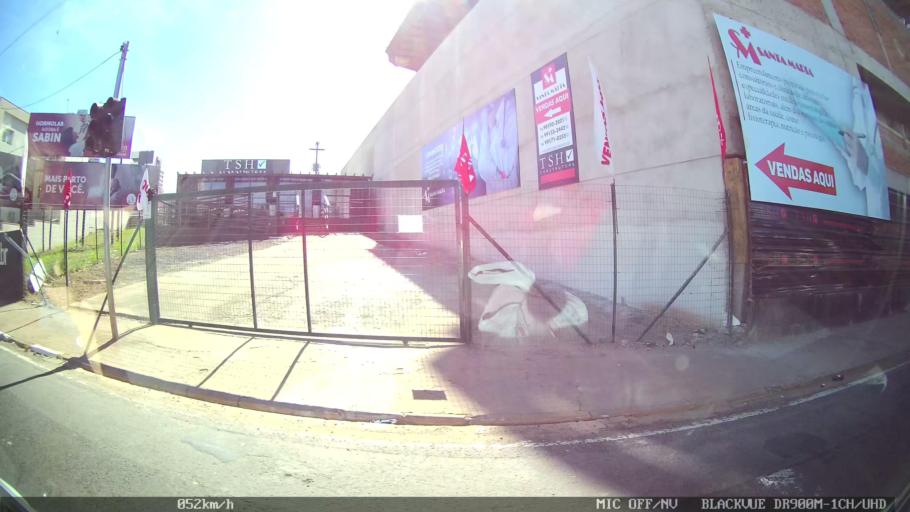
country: BR
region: Sao Paulo
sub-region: Franca
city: Franca
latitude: -20.5373
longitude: -47.3882
